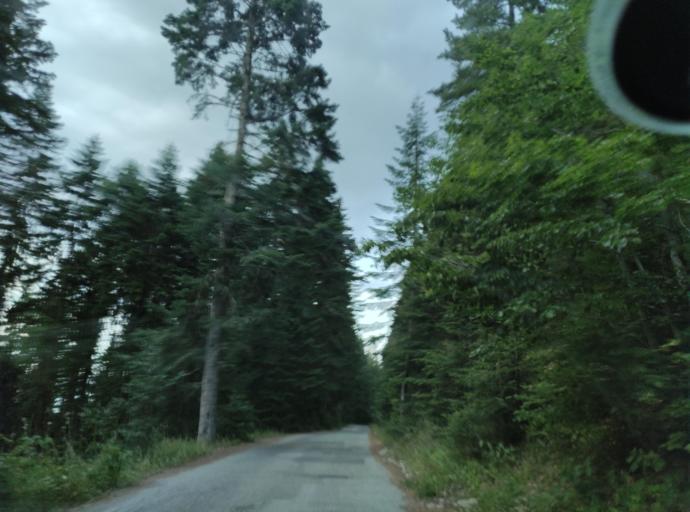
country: BG
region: Blagoevgrad
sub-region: Obshtina Bansko
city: Bansko
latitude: 41.7805
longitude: 23.4425
